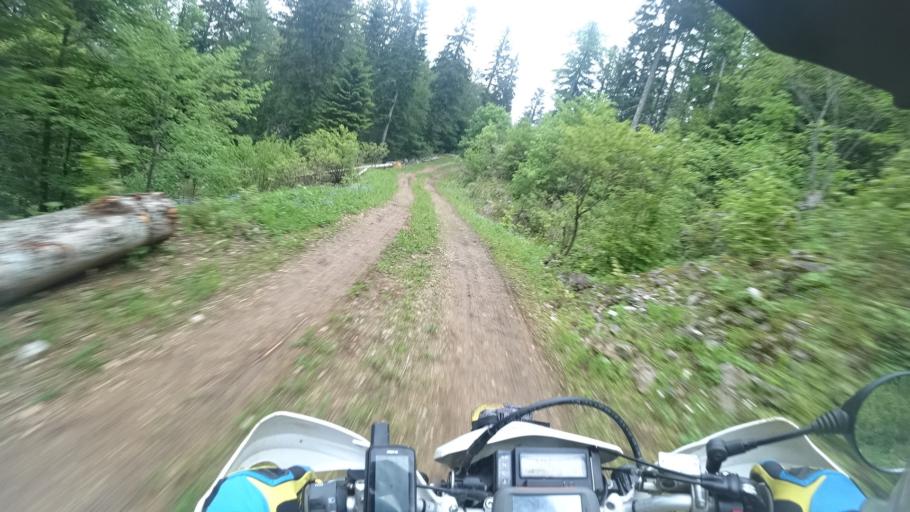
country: BA
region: Federation of Bosnia and Herzegovina
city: Bihac
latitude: 44.6271
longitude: 15.8280
